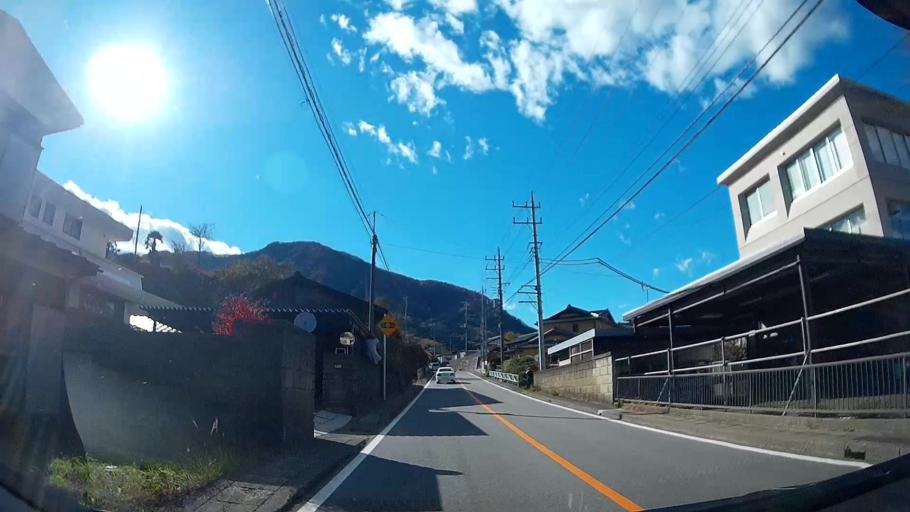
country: JP
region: Yamanashi
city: Otsuki
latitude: 35.6016
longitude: 138.9201
